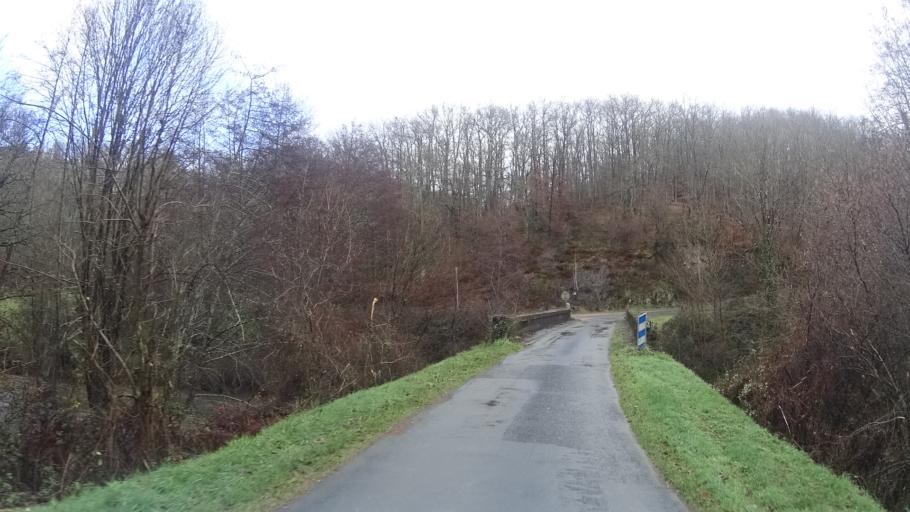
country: FR
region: Aquitaine
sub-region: Departement de la Dordogne
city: Thiviers
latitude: 45.4113
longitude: 0.9739
